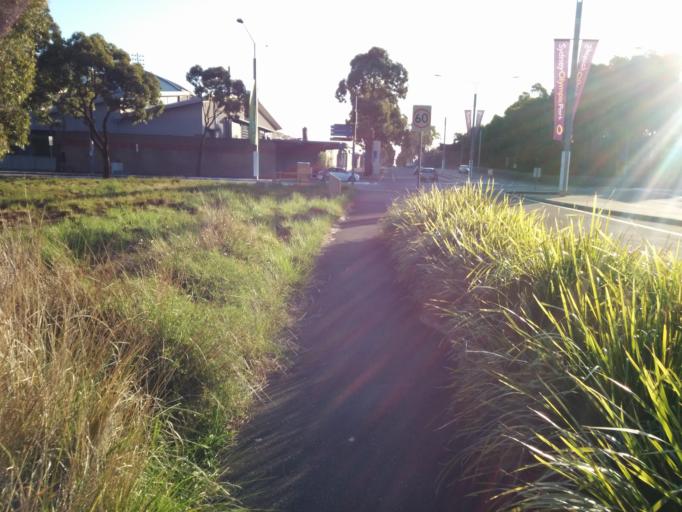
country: AU
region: New South Wales
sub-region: Canada Bay
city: Concord West
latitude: -33.8397
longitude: 151.0691
